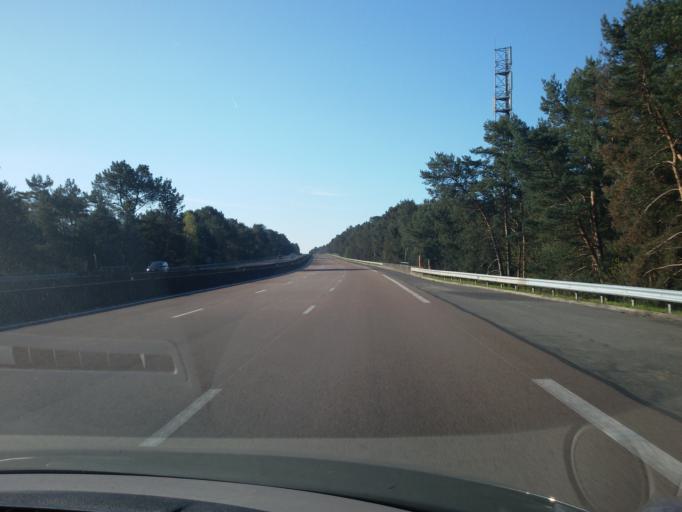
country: FR
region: Ile-de-France
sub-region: Departement de Seine-et-Marne
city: Arbonne-la-Foret
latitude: 48.3907
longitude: 2.5548
